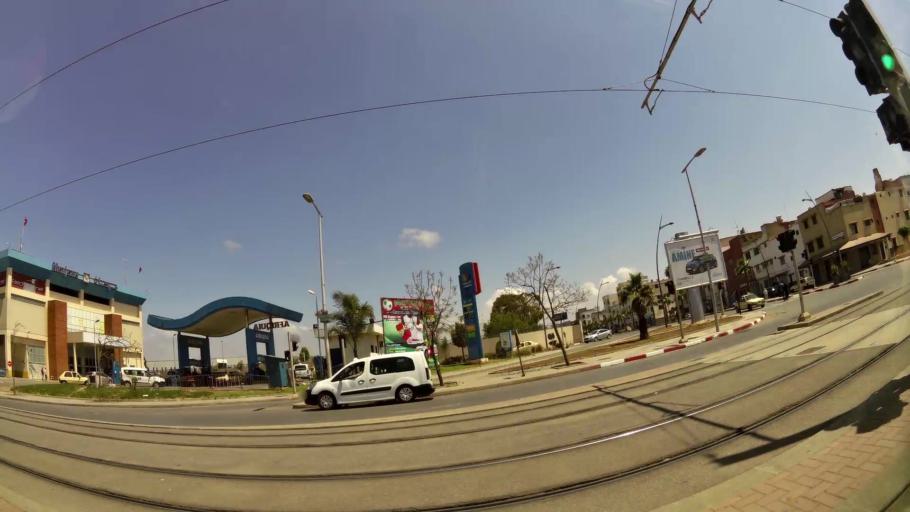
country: MA
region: Rabat-Sale-Zemmour-Zaer
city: Sale
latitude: 34.0513
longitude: -6.7972
